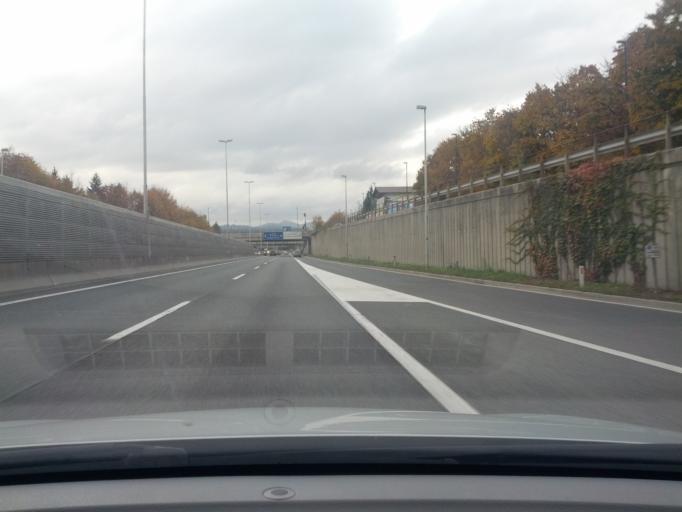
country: SI
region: Ljubljana
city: Ljubljana
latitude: 46.0839
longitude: 14.5106
